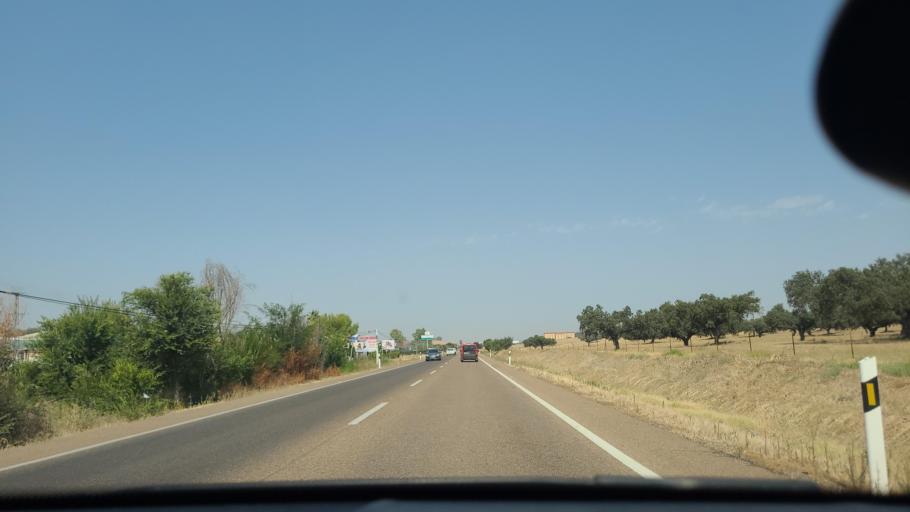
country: ES
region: Extremadura
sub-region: Provincia de Badajoz
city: Badajoz
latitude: 38.8413
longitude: -6.9298
